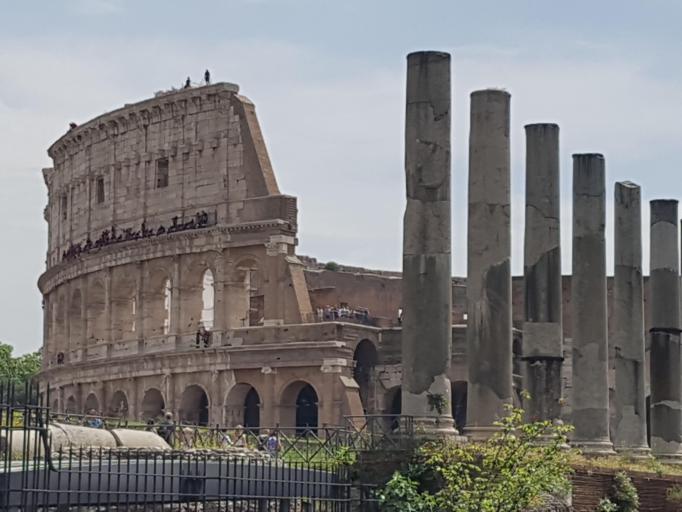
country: IT
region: Latium
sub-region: Citta metropolitana di Roma Capitale
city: Rome
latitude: 41.8903
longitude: 12.4889
